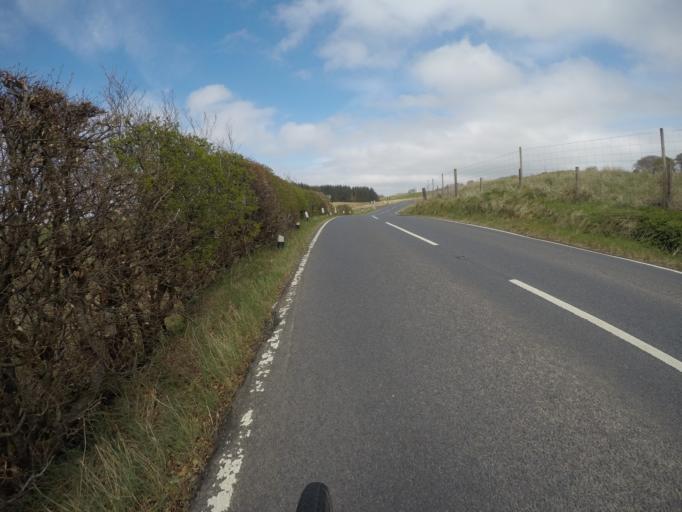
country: GB
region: Scotland
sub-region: East Renfrewshire
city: Neilston
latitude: 55.7218
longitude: -4.4308
